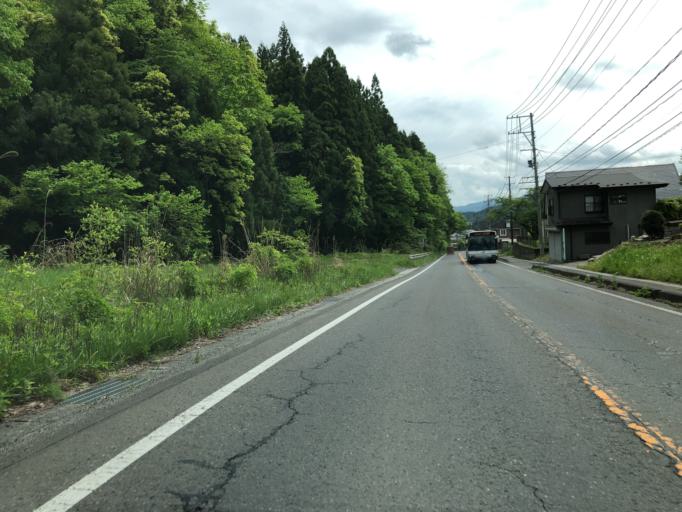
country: JP
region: Fukushima
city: Ishikawa
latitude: 37.0416
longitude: 140.3791
